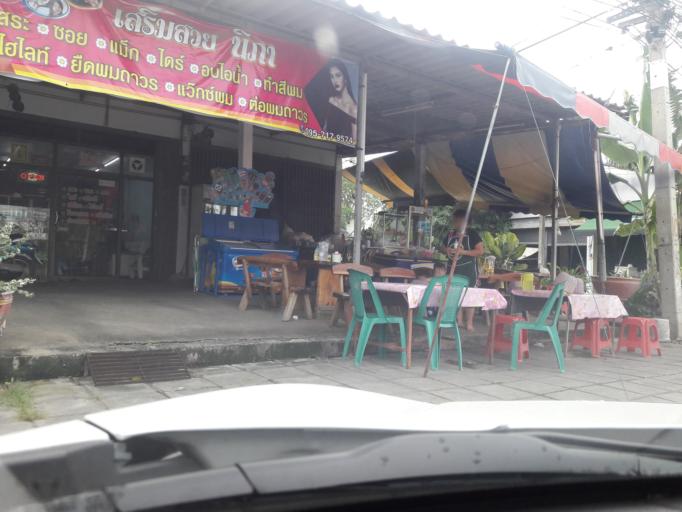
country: TH
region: Lop Buri
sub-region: Amphoe Tha Luang
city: Tha Luang
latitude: 15.0705
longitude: 101.1107
